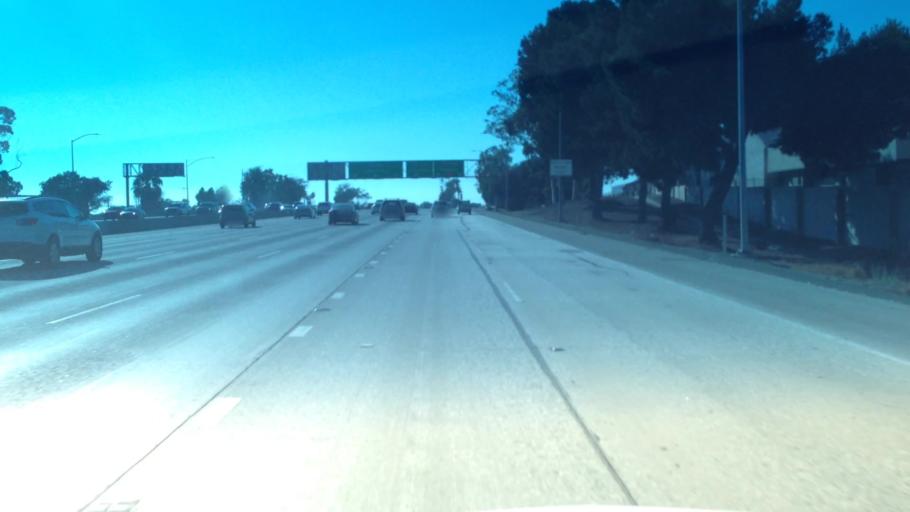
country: US
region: California
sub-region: Los Angeles County
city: Signal Hill
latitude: 33.8220
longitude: -118.1959
